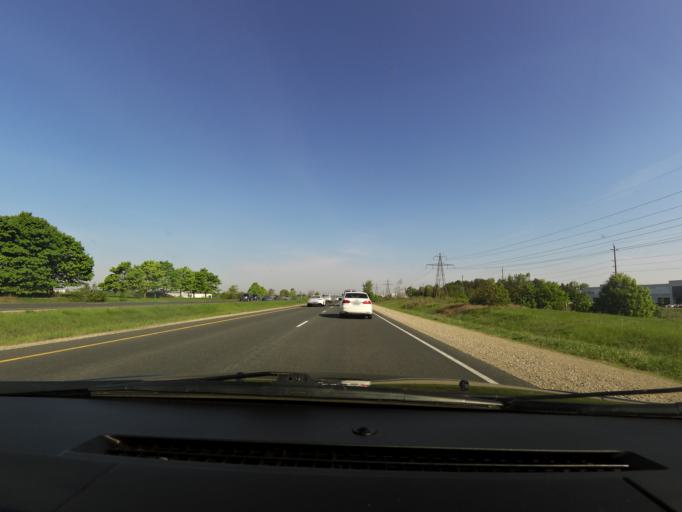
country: CA
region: Ontario
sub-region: Wellington County
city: Guelph
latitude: 43.4824
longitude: -80.2017
